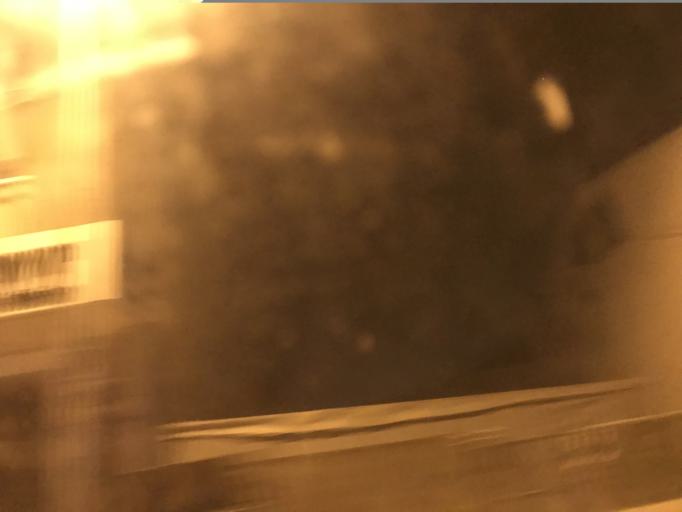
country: TR
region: Istanbul
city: Pendik
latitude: 40.8986
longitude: 29.2675
